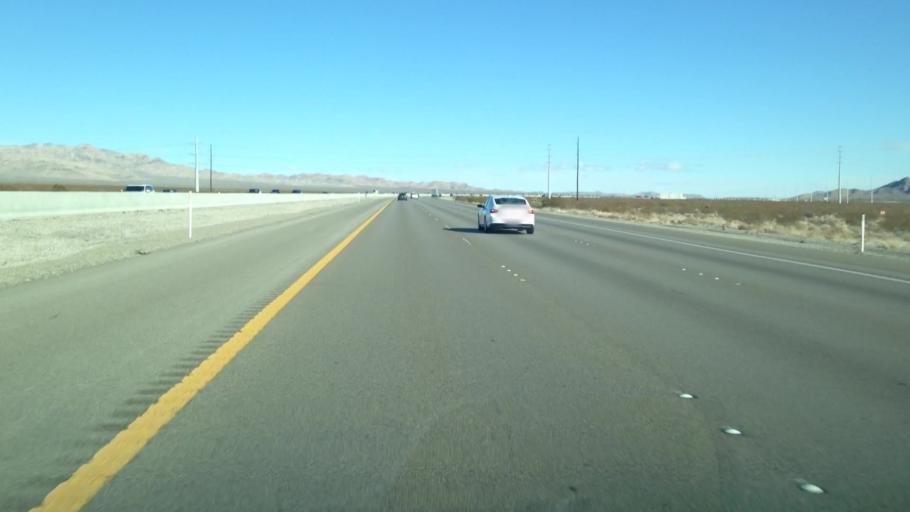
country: US
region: Nevada
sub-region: Clark County
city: Sandy Valley
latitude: 35.7391
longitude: -115.3566
